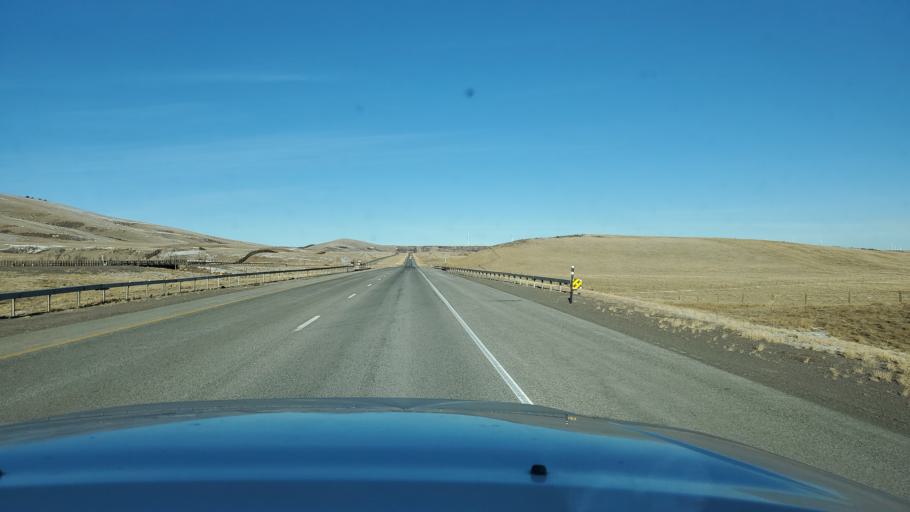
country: US
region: Wyoming
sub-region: Albany County
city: Laramie
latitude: 41.5737
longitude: -106.1545
